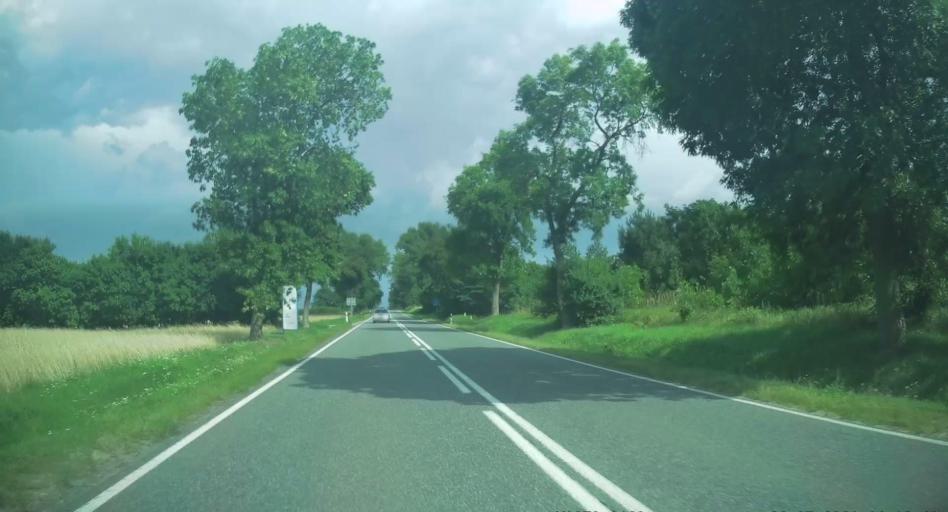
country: PL
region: Lodz Voivodeship
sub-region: Powiat brzezinski
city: Jezow
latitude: 51.8106
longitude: 19.9943
